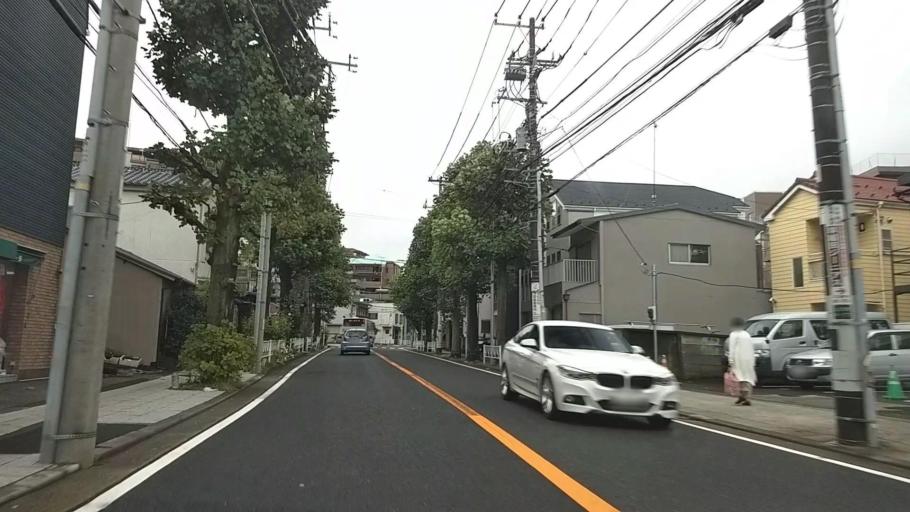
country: JP
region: Kanagawa
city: Yokohama
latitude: 35.4269
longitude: 139.6397
